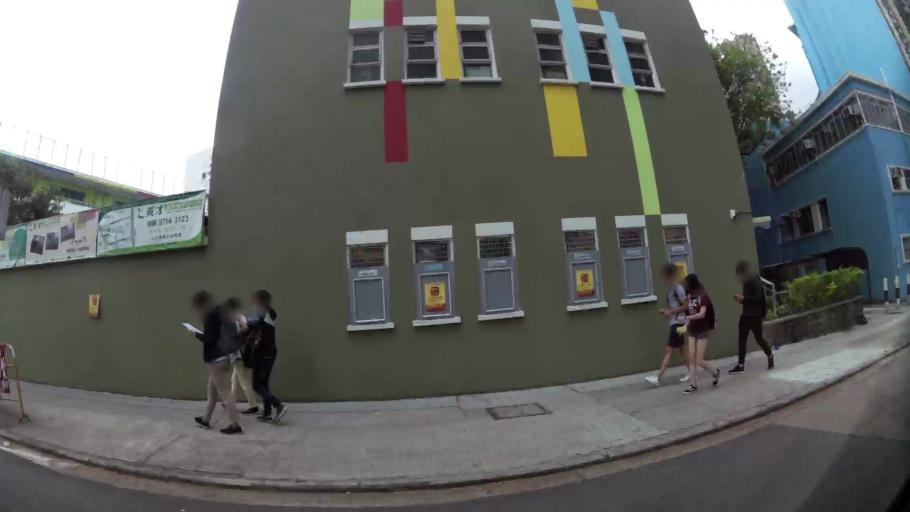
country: HK
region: Kowloon City
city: Kowloon
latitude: 22.3205
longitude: 114.1854
